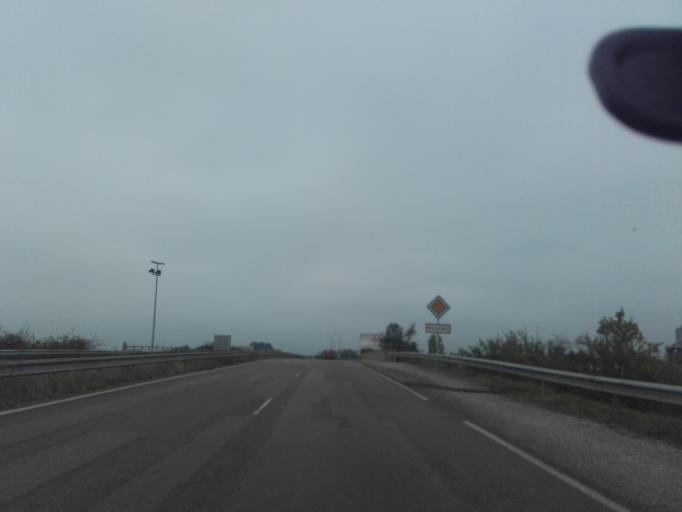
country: FR
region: Bourgogne
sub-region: Departement de la Cote-d'Or
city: Beaune
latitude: 47.0419
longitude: 4.8486
